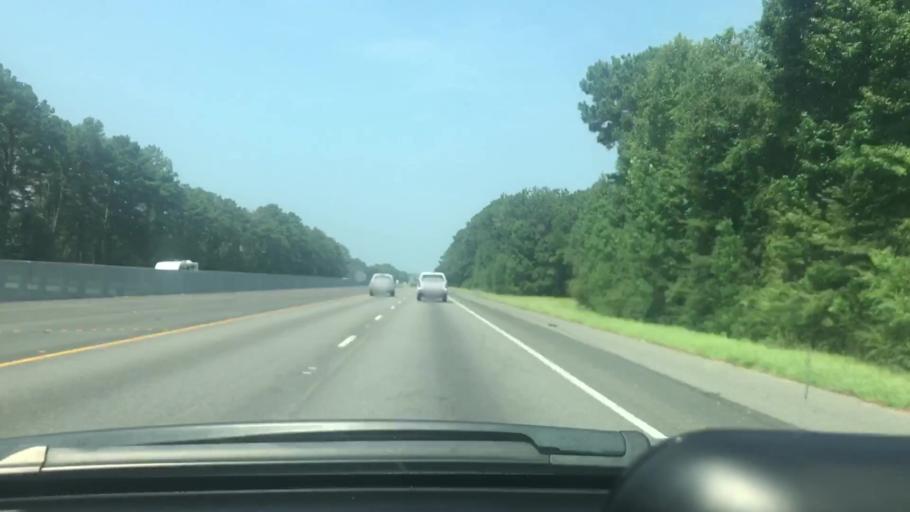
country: US
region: Louisiana
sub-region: Livingston Parish
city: Albany
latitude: 30.4764
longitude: -90.5985
